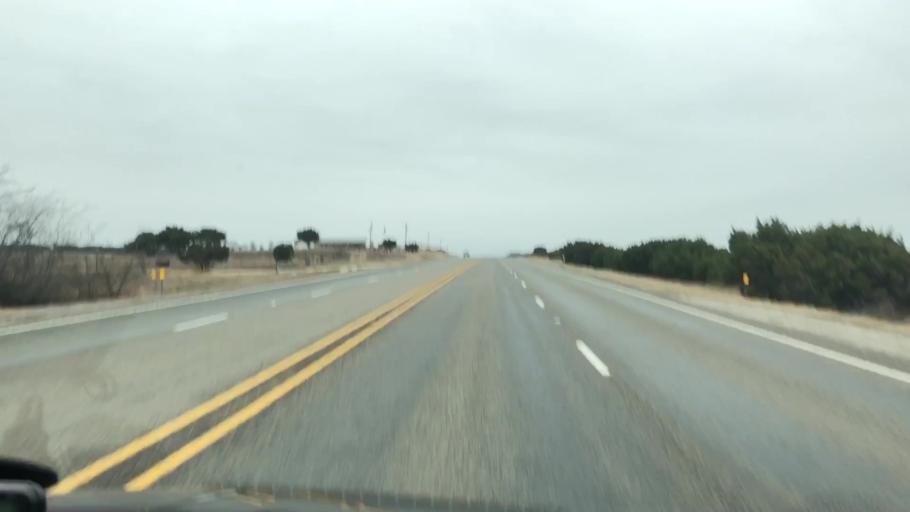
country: US
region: Texas
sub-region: Lampasas County
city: Lampasas
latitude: 31.1815
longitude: -98.1730
